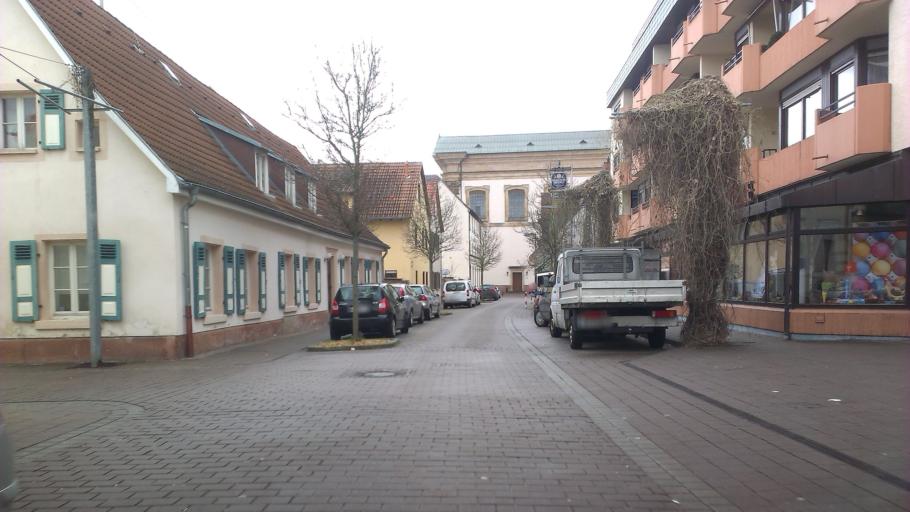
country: DE
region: Rheinland-Pfalz
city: Gartenstadt
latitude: 49.4911
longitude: 8.3759
